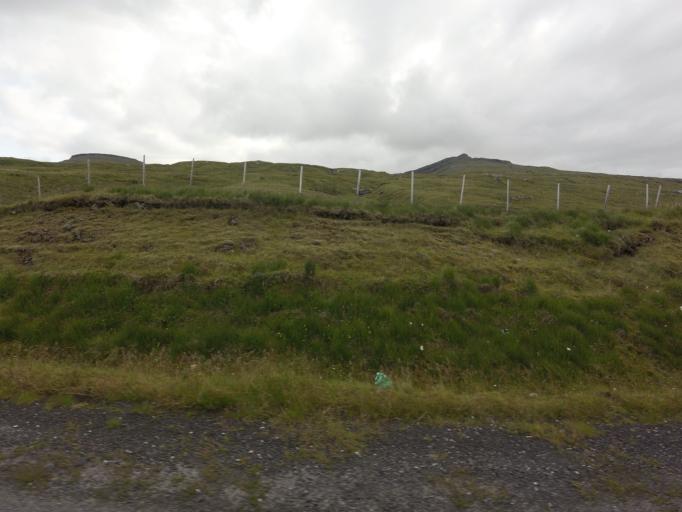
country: FO
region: Eysturoy
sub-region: Eidi
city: Eidi
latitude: 62.2152
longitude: -6.9964
